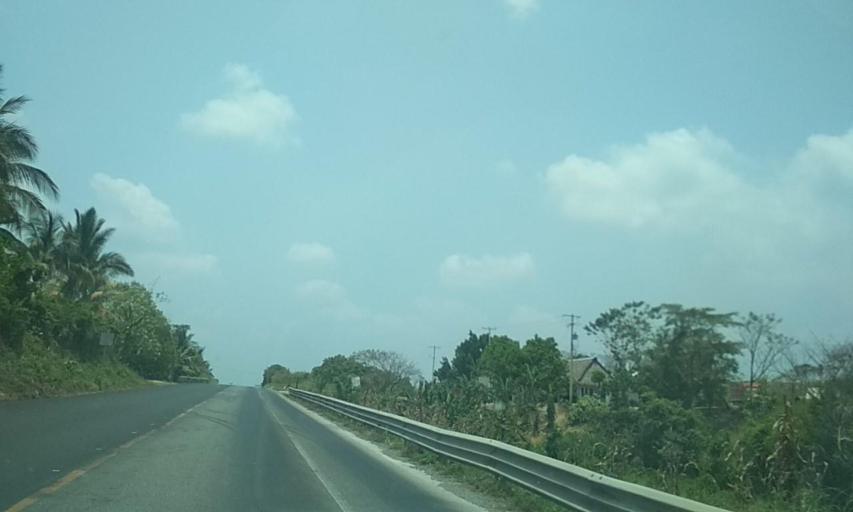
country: MX
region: Tabasco
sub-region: Huimanguillo
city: Francisco Rueda
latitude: 17.7154
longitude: -93.9469
